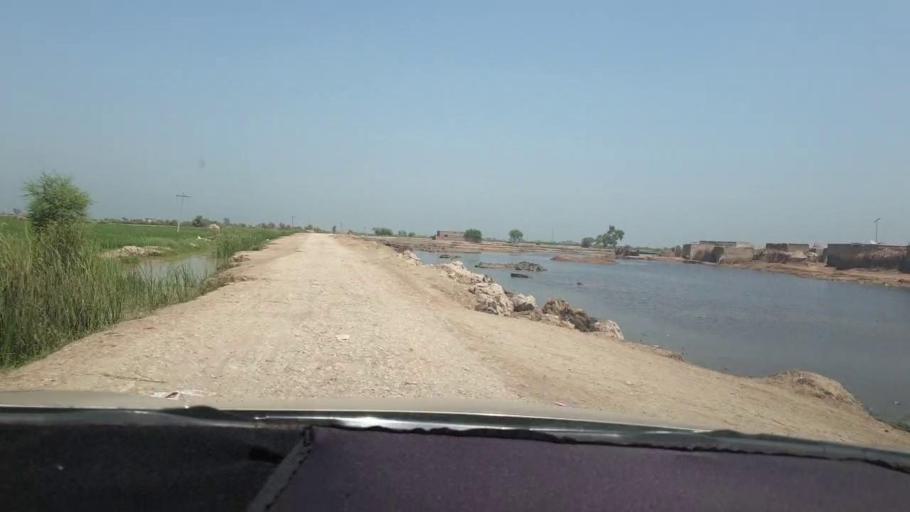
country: PK
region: Sindh
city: Shahdadkot
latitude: 27.8397
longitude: 68.0026
